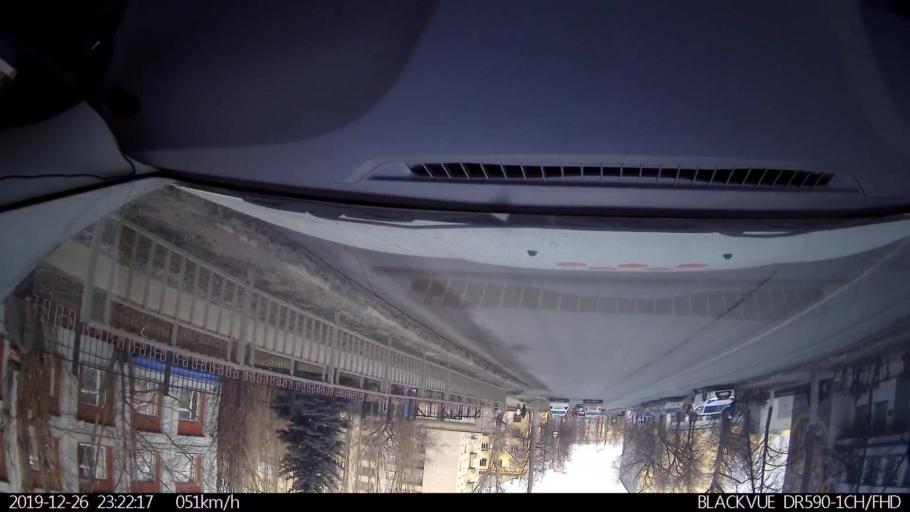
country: RU
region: Nizjnij Novgorod
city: Gorbatovka
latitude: 56.2410
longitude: 43.8686
